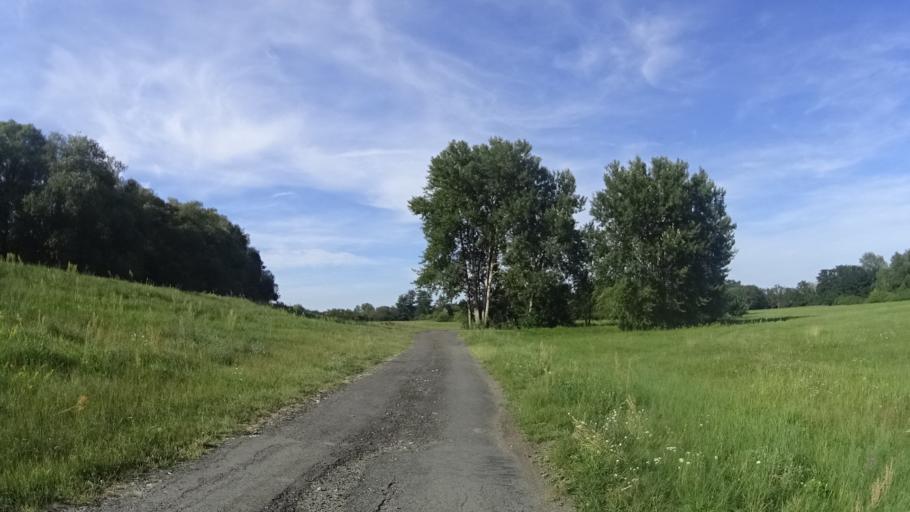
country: AT
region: Lower Austria
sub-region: Politischer Bezirk Ganserndorf
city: Drosing
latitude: 48.5472
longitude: 16.9628
